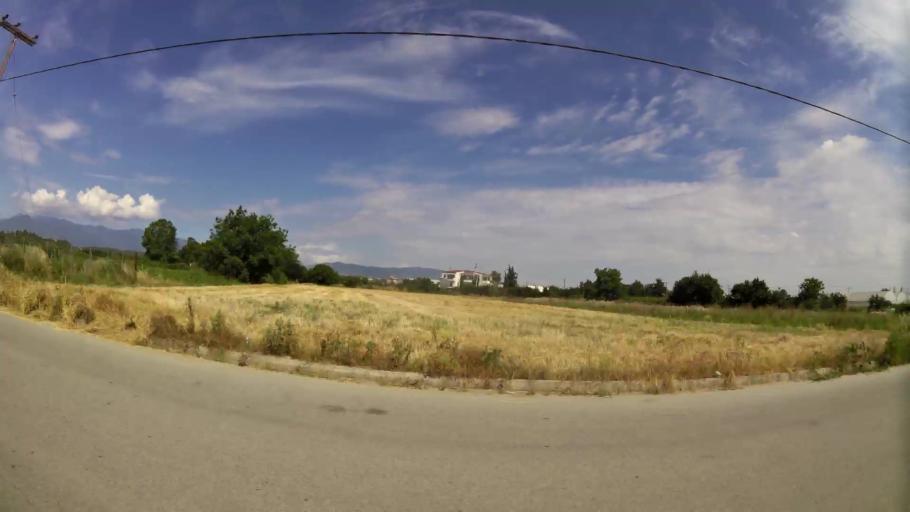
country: GR
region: Central Macedonia
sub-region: Nomos Pierias
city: Katerini
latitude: 40.2794
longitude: 22.4871
